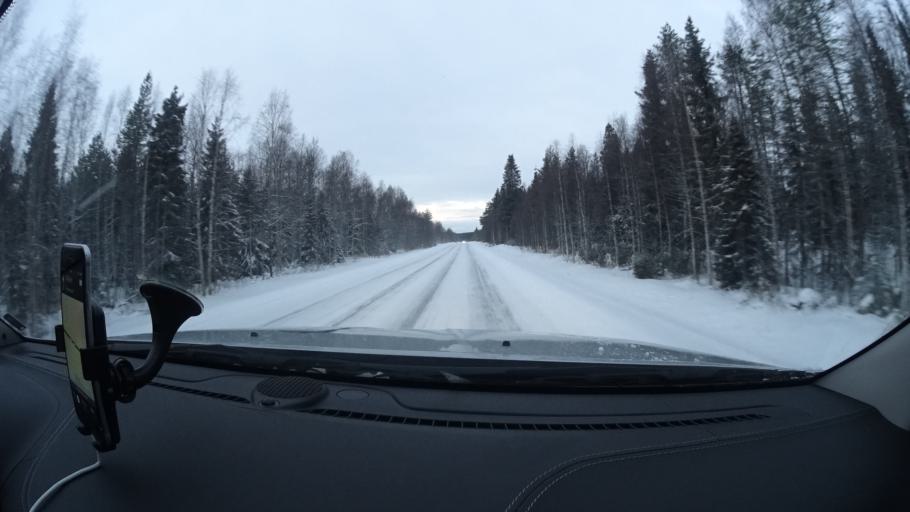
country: FI
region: Lapland
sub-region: Itae-Lappi
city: Posio
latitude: 66.0928
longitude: 28.6442
